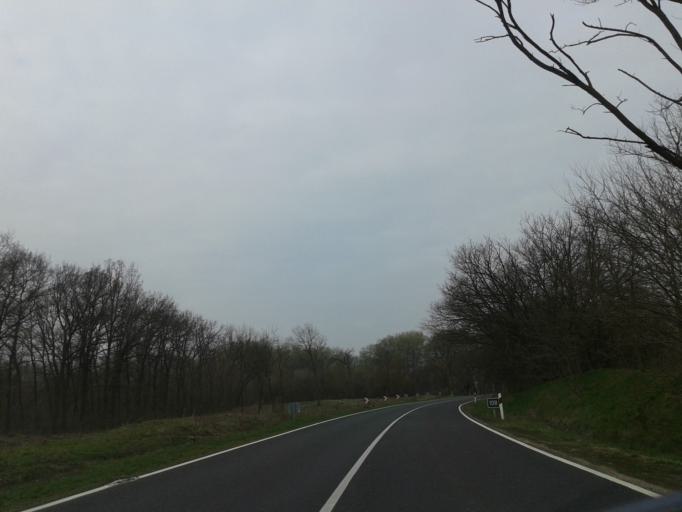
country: HU
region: Gyor-Moson-Sopron
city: Bony
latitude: 47.7316
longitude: 17.8499
